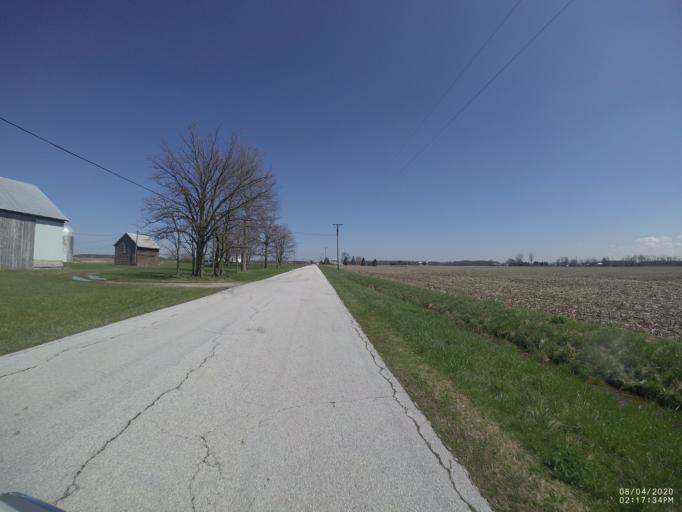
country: US
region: Ohio
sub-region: Sandusky County
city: Stony Prairie
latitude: 41.2821
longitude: -83.2421
